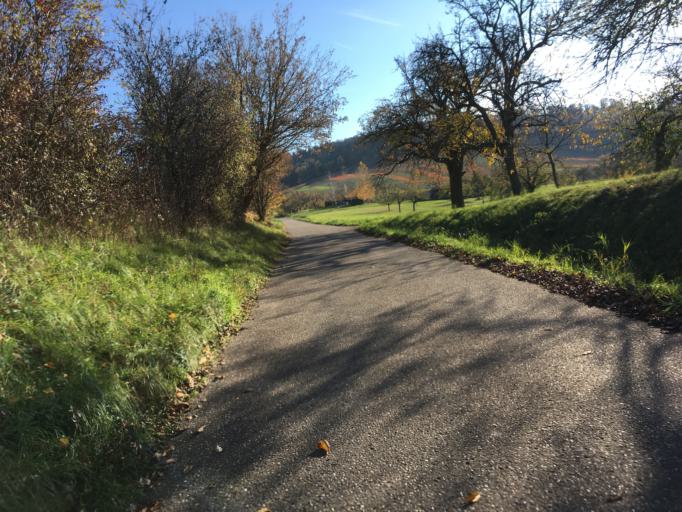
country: DE
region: Baden-Wuerttemberg
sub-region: Karlsruhe Region
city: Oberderdingen
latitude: 49.0545
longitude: 8.8051
